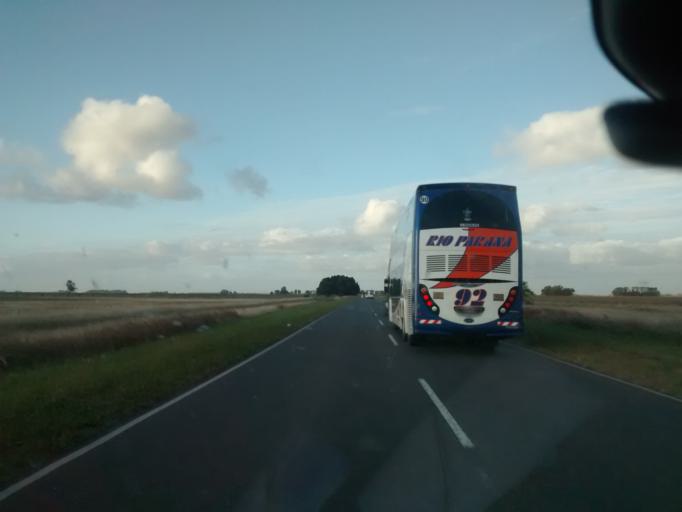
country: AR
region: Buenos Aires
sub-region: Partido de General Belgrano
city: General Belgrano
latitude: -35.8555
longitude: -58.6068
